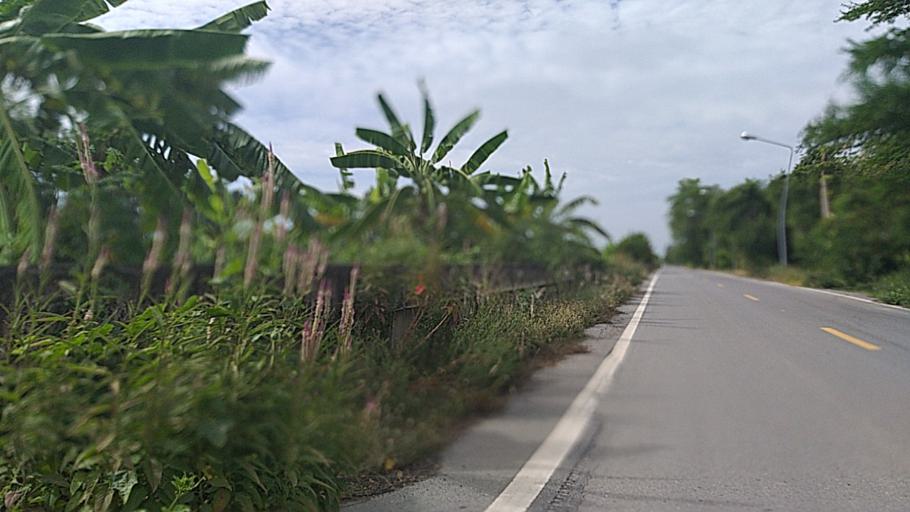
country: TH
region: Pathum Thani
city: Nong Suea
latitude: 14.0577
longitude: 100.8925
